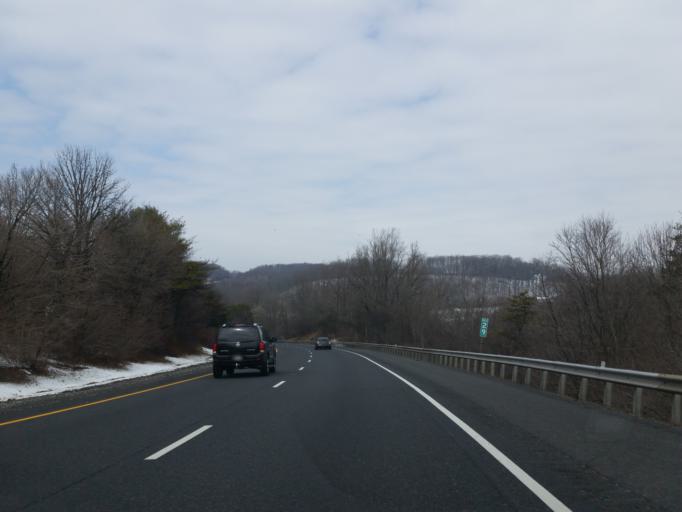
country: US
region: Maryland
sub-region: Baltimore County
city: Hunt Valley
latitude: 39.6102
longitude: -76.6581
